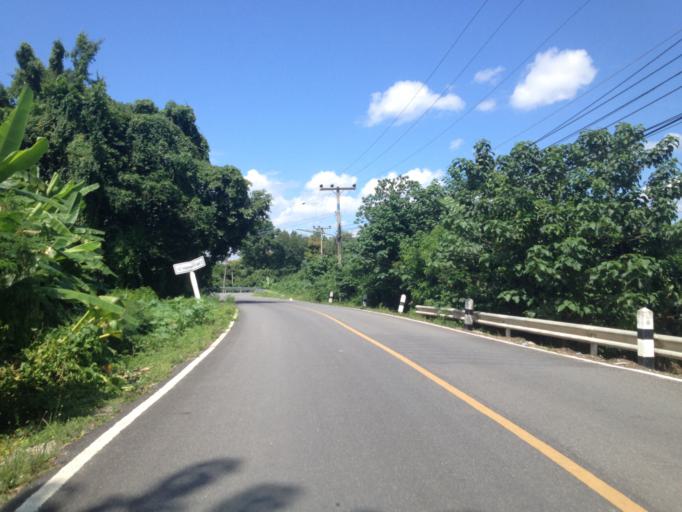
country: TH
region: Chiang Mai
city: Hang Dong
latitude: 18.6605
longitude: 98.9636
